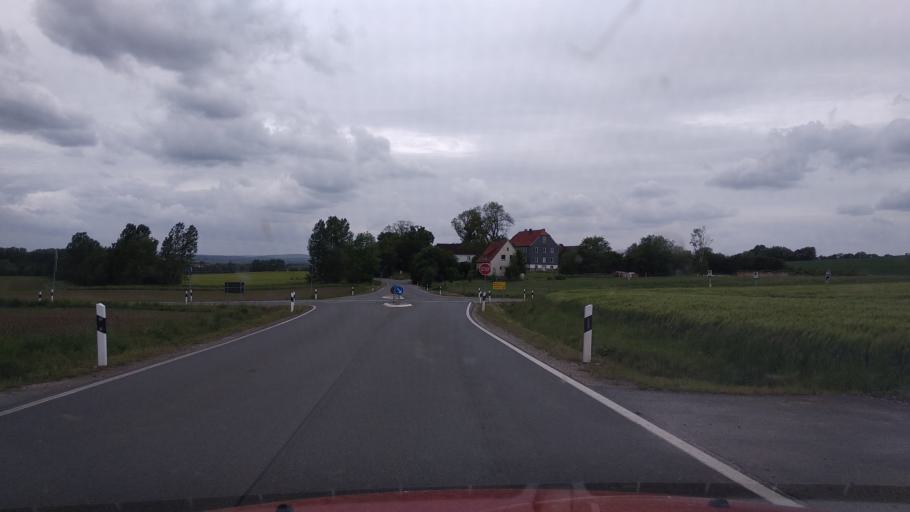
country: DE
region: North Rhine-Westphalia
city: Borgentreich
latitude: 51.5404
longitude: 9.2462
